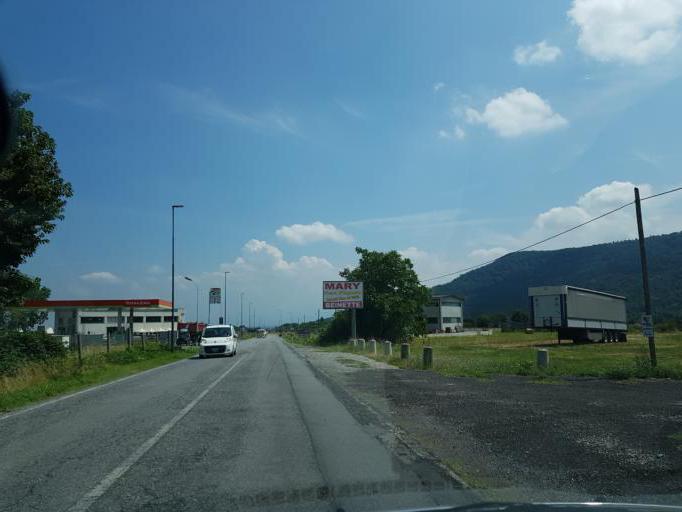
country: IT
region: Piedmont
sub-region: Provincia di Cuneo
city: Montemale di Cuneo
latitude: 44.4550
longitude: 7.3839
